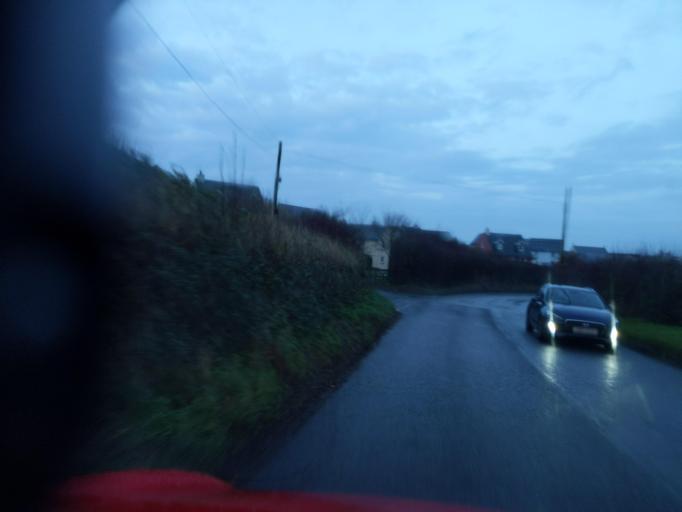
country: GB
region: England
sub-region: Plymouth
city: Plymstock
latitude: 50.3483
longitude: -4.0779
